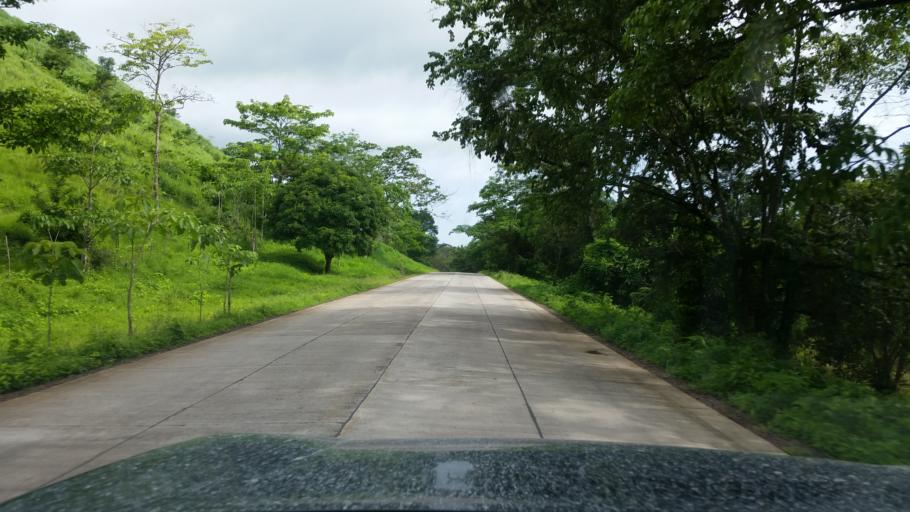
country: NI
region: Atlantico Norte (RAAN)
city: Siuna
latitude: 13.5415
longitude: -84.8239
